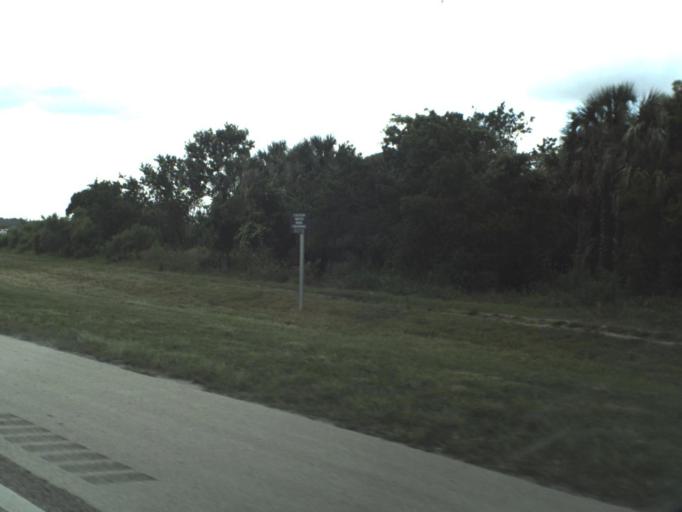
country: US
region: Florida
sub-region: Brevard County
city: Cocoa
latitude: 28.4044
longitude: -80.7246
